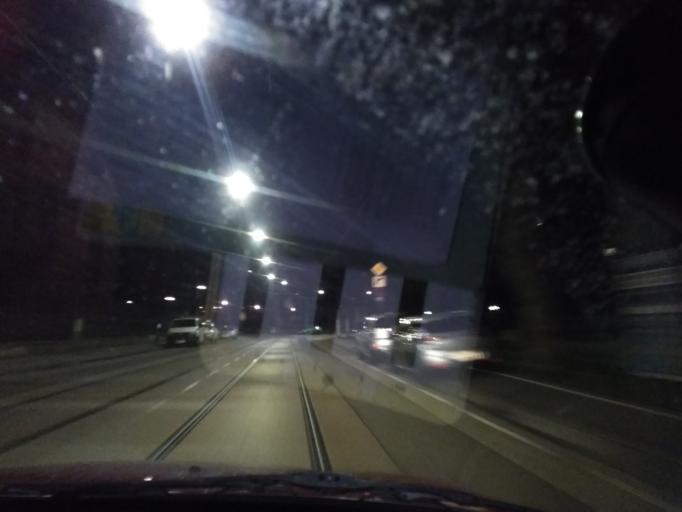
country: AT
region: Lower Austria
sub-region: Politischer Bezirk Modling
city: Perchtoldsdorf
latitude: 48.1836
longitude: 16.2930
